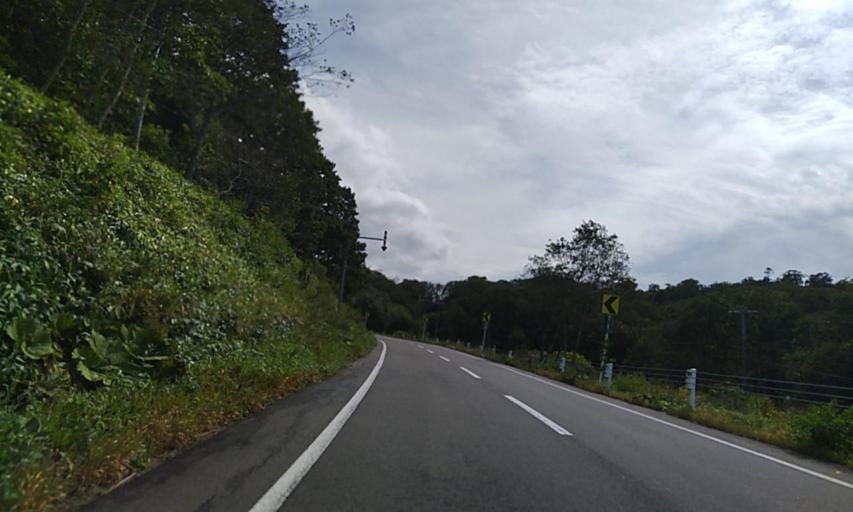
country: JP
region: Hokkaido
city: Kushiro
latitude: 42.8410
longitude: 143.8400
